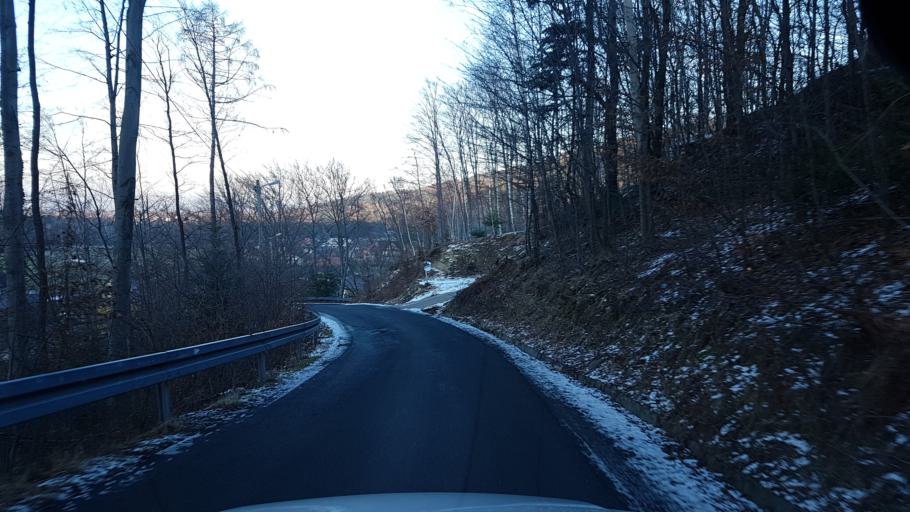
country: PL
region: Lesser Poland Voivodeship
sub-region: Powiat nowosadecki
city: Rytro
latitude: 49.5174
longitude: 20.6621
